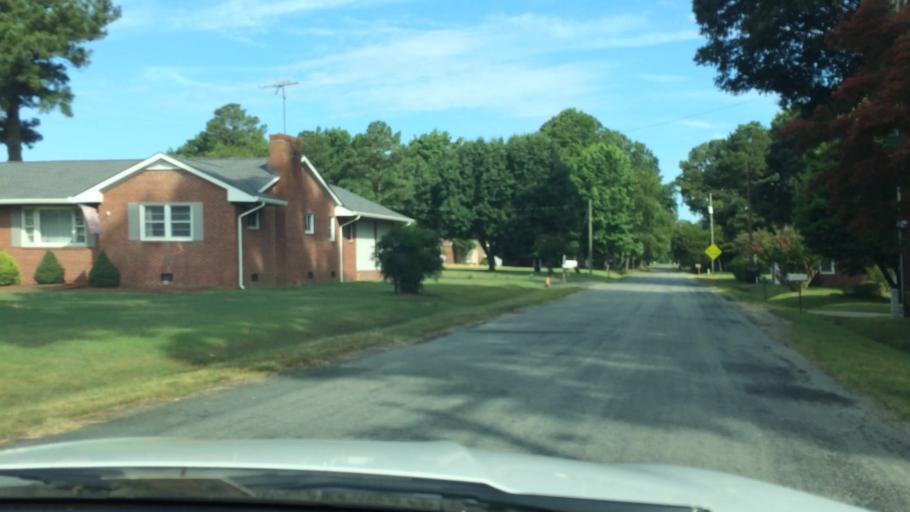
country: US
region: Virginia
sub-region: King William County
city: West Point
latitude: 37.5209
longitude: -76.8304
